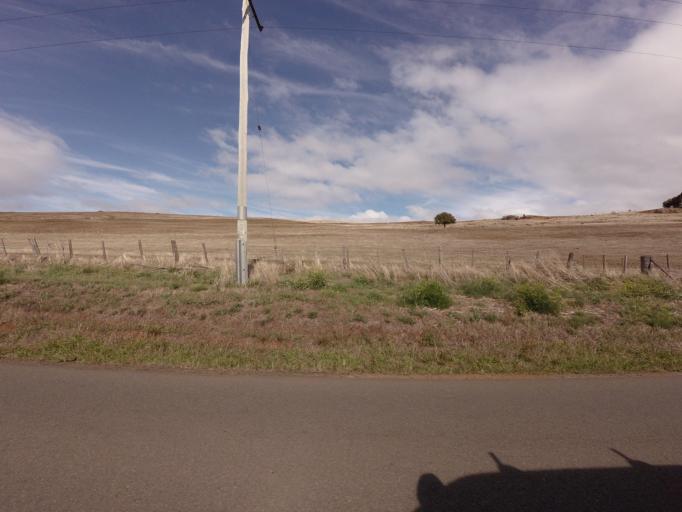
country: AU
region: Tasmania
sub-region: Derwent Valley
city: New Norfolk
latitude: -42.6975
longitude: 146.9302
